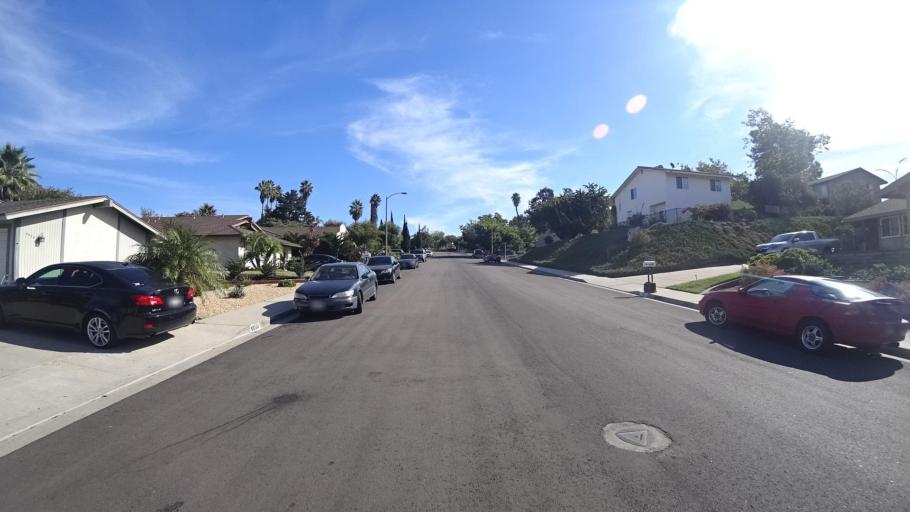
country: US
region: California
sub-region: San Diego County
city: Spring Valley
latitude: 32.7274
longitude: -116.9818
